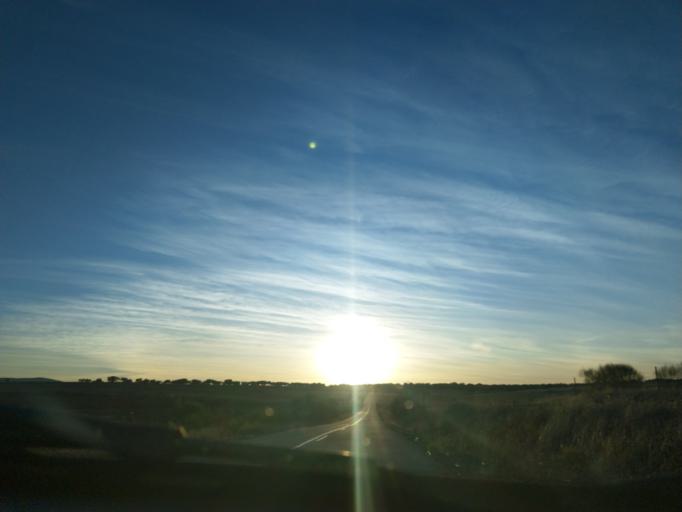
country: ES
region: Extremadura
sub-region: Provincia de Badajoz
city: Valverde de Llerena
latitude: 38.2069
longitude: -5.8345
